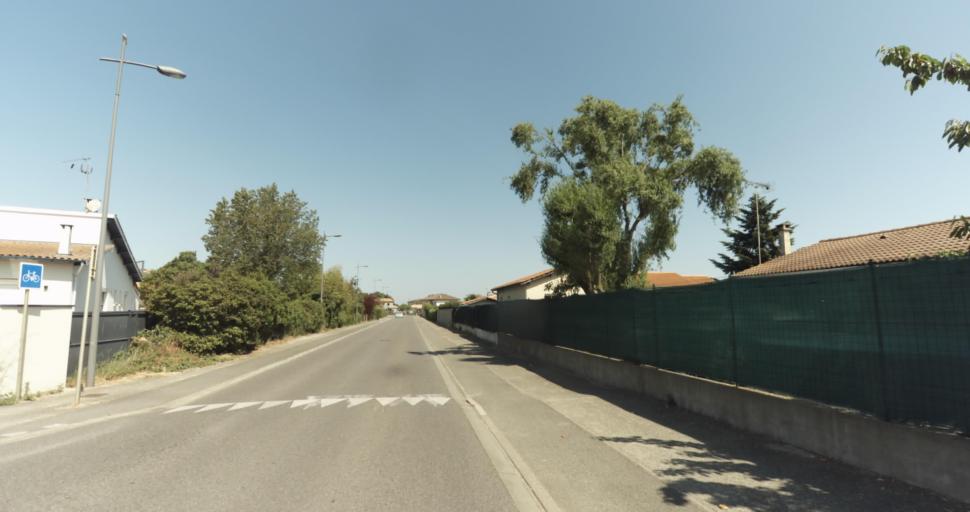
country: FR
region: Midi-Pyrenees
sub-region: Departement de la Haute-Garonne
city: Plaisance-du-Touch
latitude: 43.5768
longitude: 1.2893
